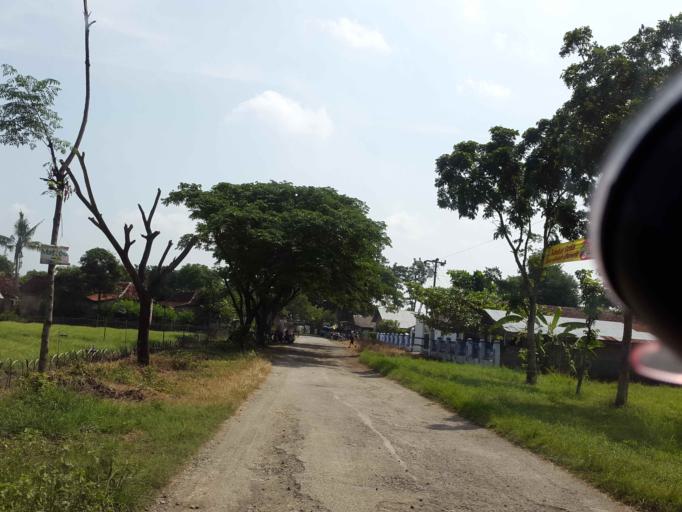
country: ID
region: Central Java
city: Pemalang
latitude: -6.9490
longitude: 109.3378
